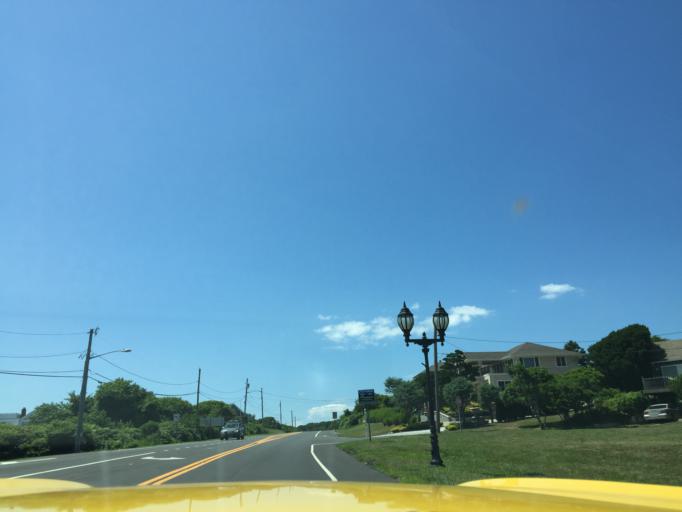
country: US
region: New York
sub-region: Suffolk County
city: Montauk
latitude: 41.0310
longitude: -71.9546
